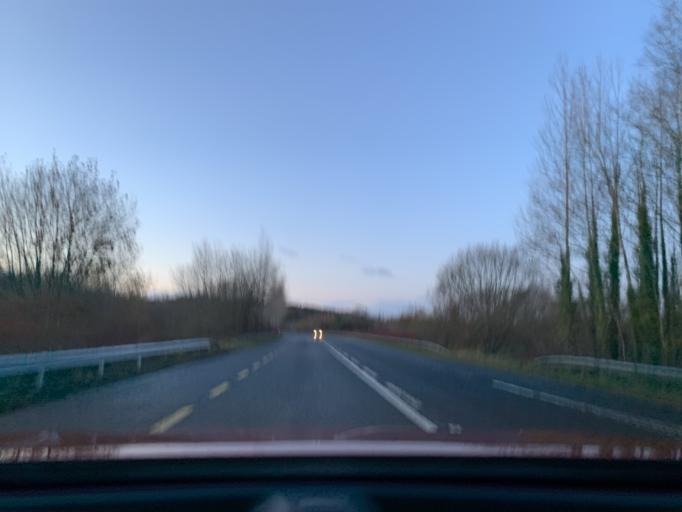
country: IE
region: Connaught
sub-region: County Leitrim
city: Carrick-on-Shannon
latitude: 53.9324
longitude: -8.0044
